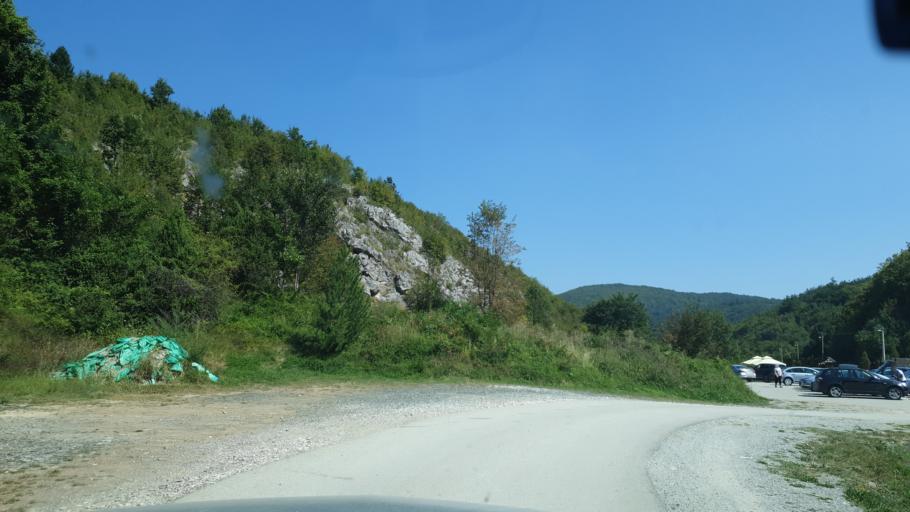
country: RS
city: Zlatibor
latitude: 43.6550
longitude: 19.8327
